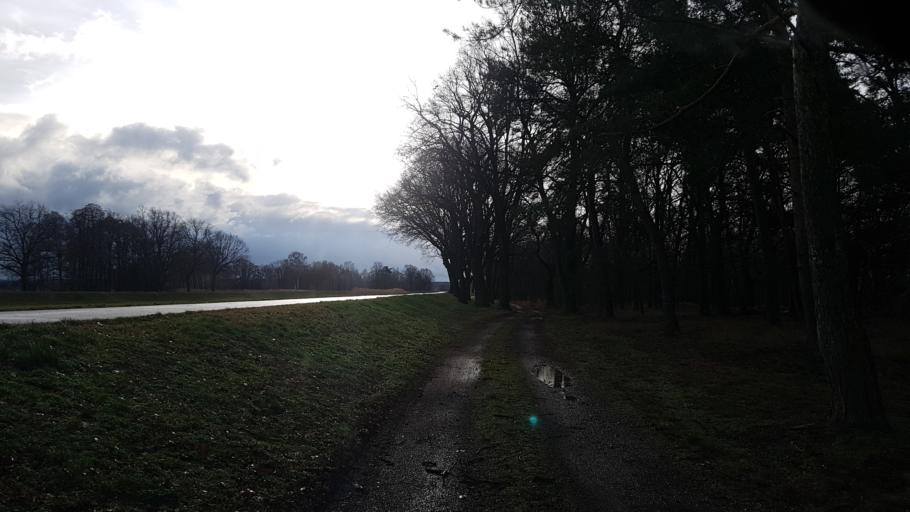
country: DE
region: Brandenburg
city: Herzberg
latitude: 51.6704
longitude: 13.2574
